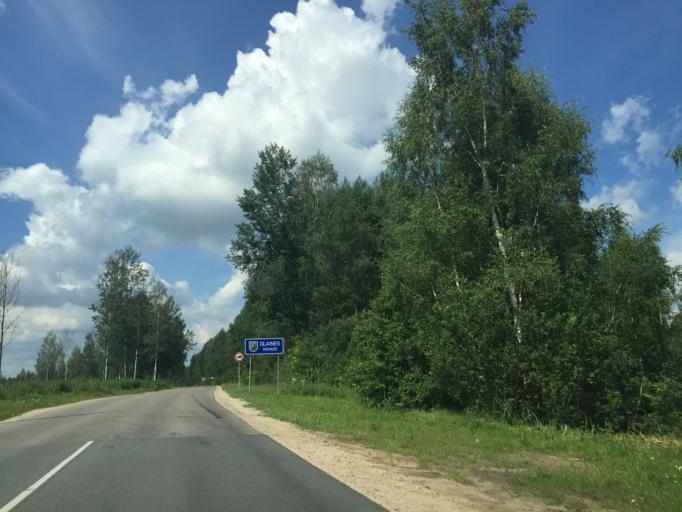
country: LV
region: Kekava
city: Balozi
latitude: 56.8665
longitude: 24.1033
